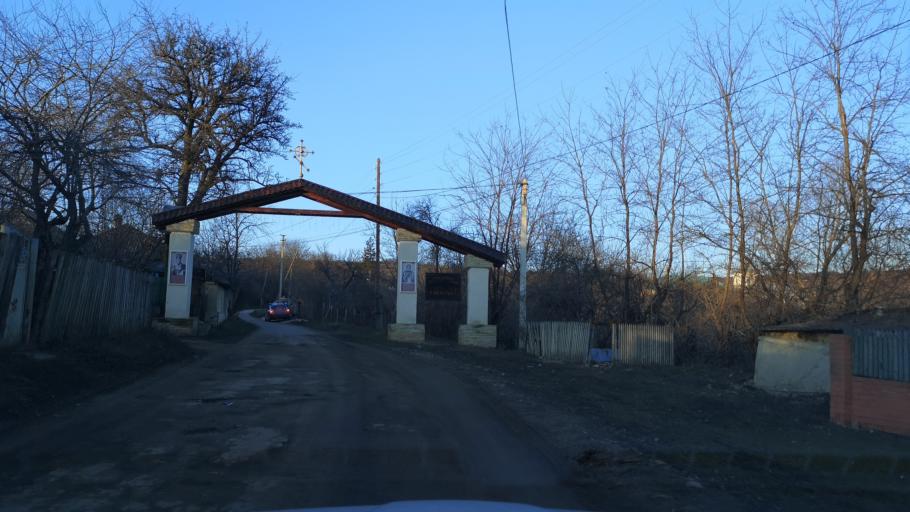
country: MD
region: Orhei
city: Orhei
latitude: 47.3661
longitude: 28.6904
